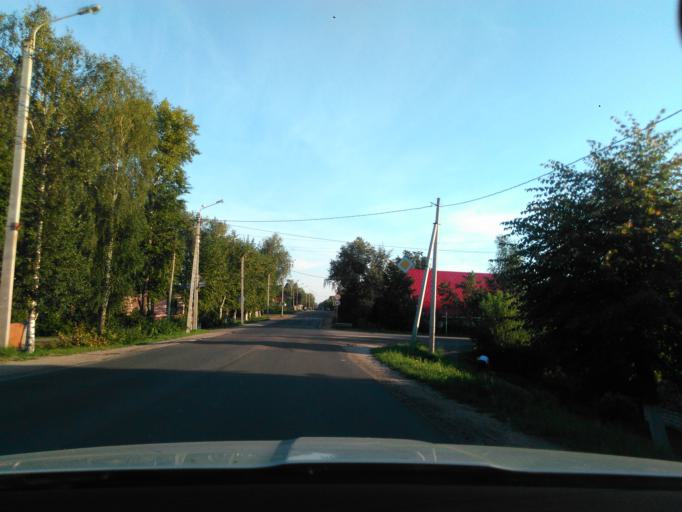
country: RU
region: Tverskaya
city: Konakovo
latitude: 56.7000
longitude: 36.7674
